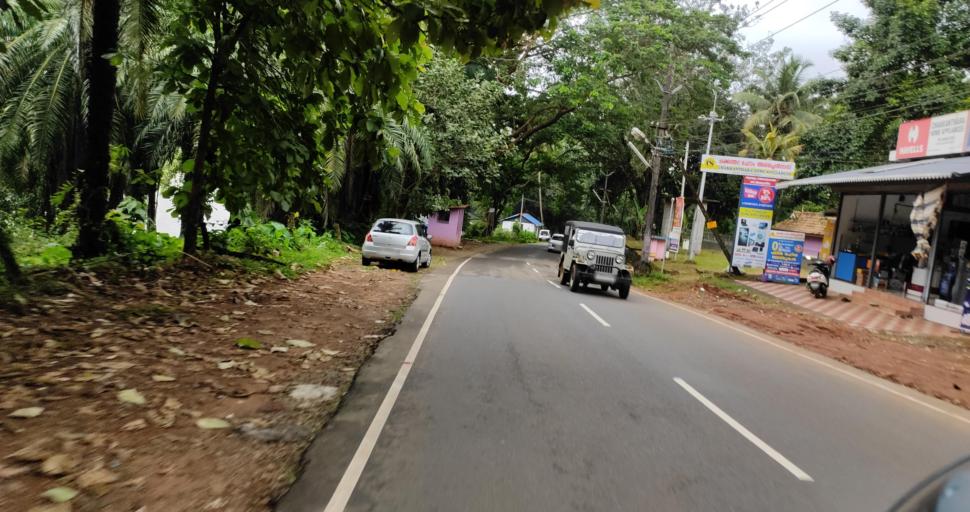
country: IN
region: Kerala
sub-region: Ernakulam
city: Angamali
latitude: 10.2945
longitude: 76.4919
